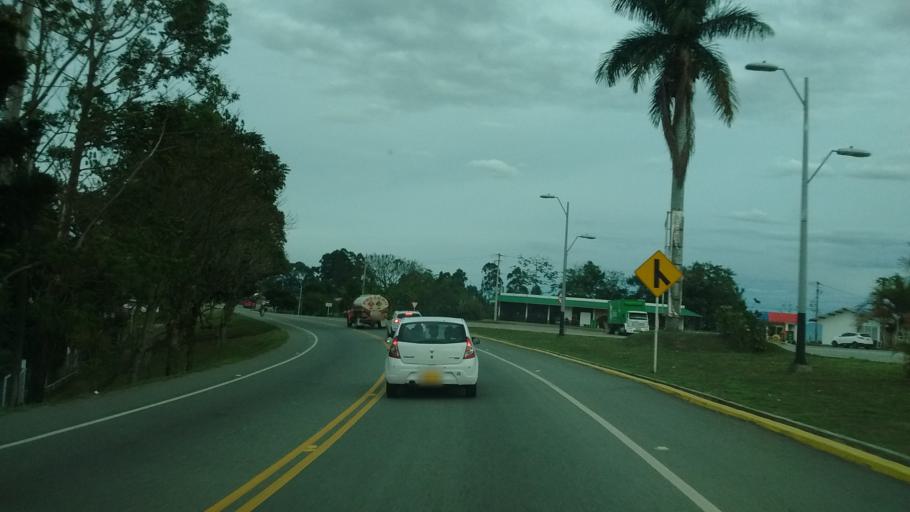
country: CO
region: Cauca
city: Cajibio
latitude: 2.6991
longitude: -76.5339
